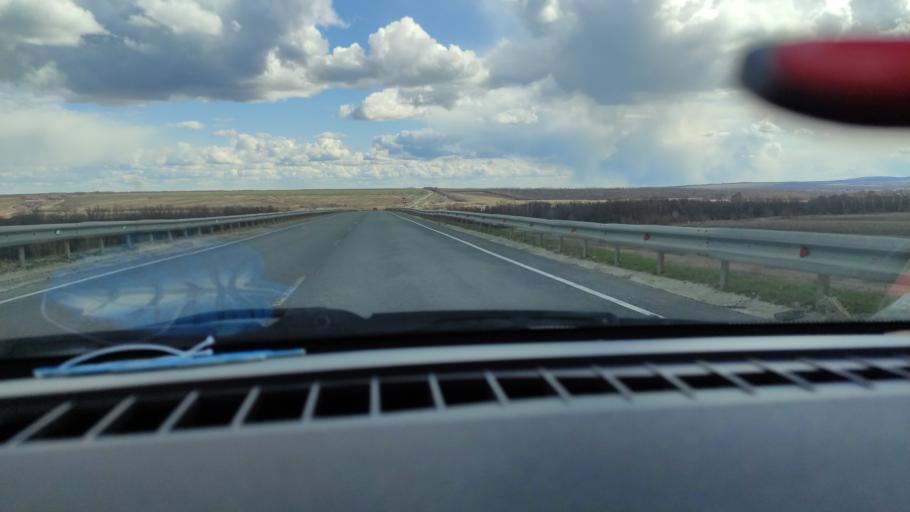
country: RU
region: Saratov
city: Dukhovnitskoye
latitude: 52.7498
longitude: 48.2488
